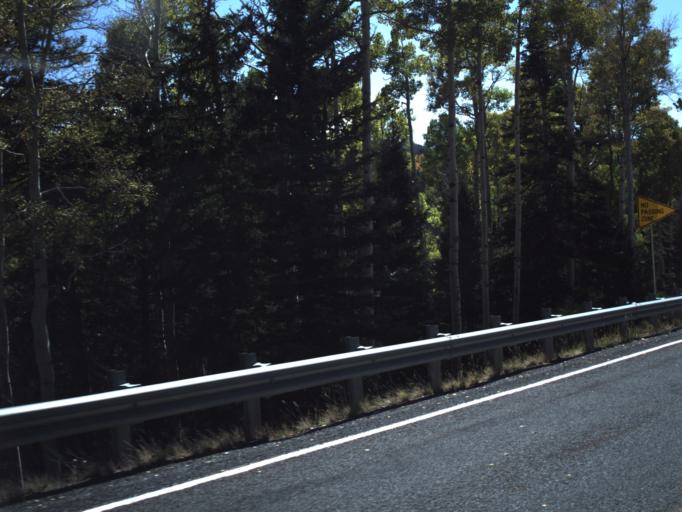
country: US
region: Utah
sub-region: Piute County
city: Junction
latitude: 38.3100
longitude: -112.4029
